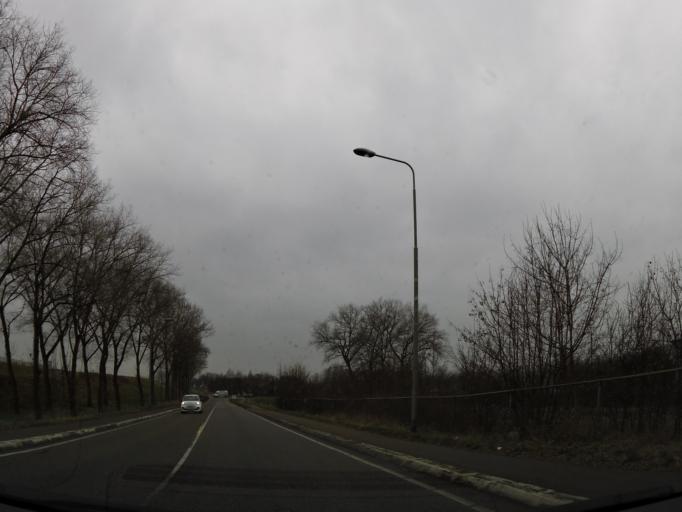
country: NL
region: Limburg
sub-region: Gemeente Maasgouw
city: Maasbracht
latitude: 51.1427
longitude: 5.8771
